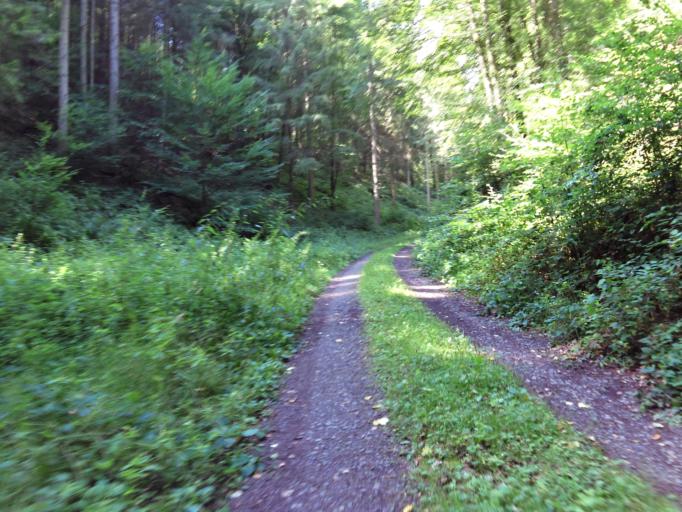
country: DE
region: Rheinland-Pfalz
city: Fischbach
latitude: 49.4110
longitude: 7.9354
